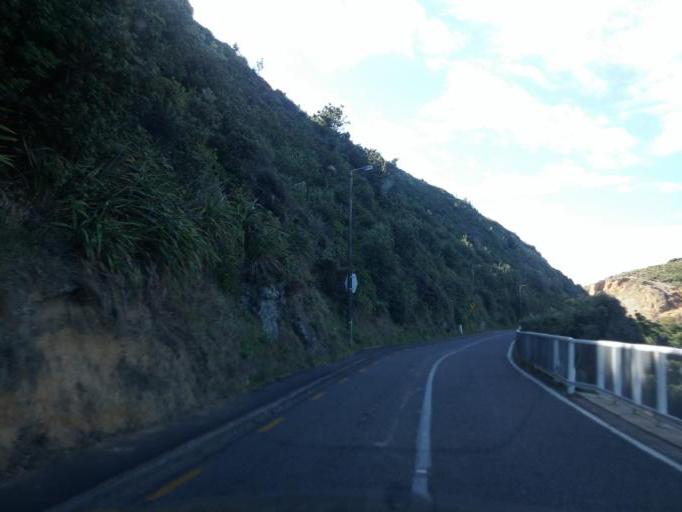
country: NZ
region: Wellington
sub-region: Wellington City
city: Wellington
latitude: -41.3307
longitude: 174.8305
